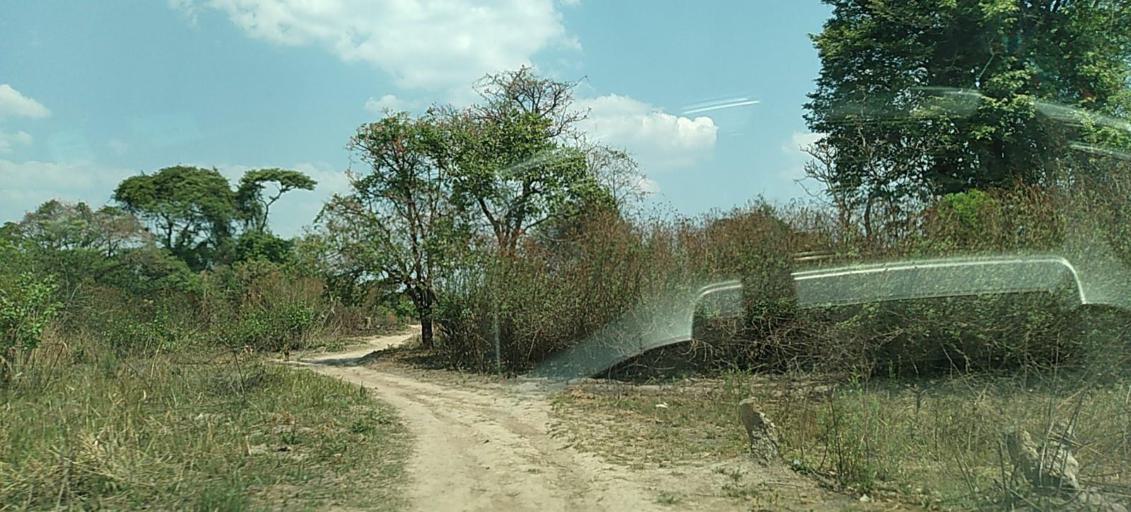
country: CD
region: Katanga
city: Kipushi
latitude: -11.9957
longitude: 27.4187
